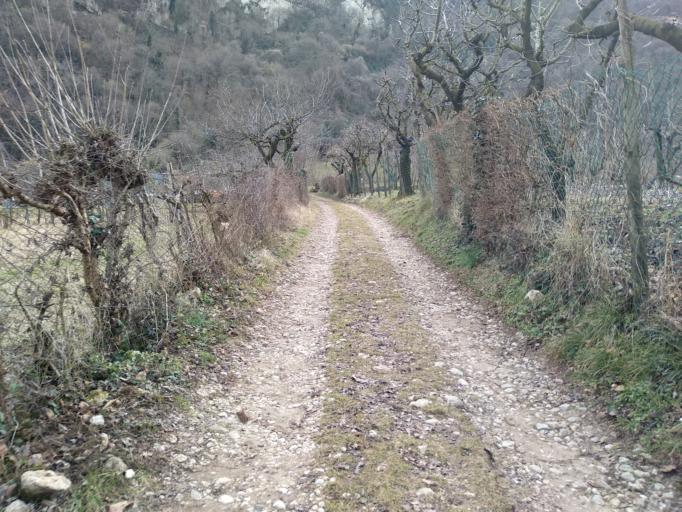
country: IT
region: Veneto
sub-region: Provincia di Vicenza
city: Lumignano
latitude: 45.4575
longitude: 11.5795
